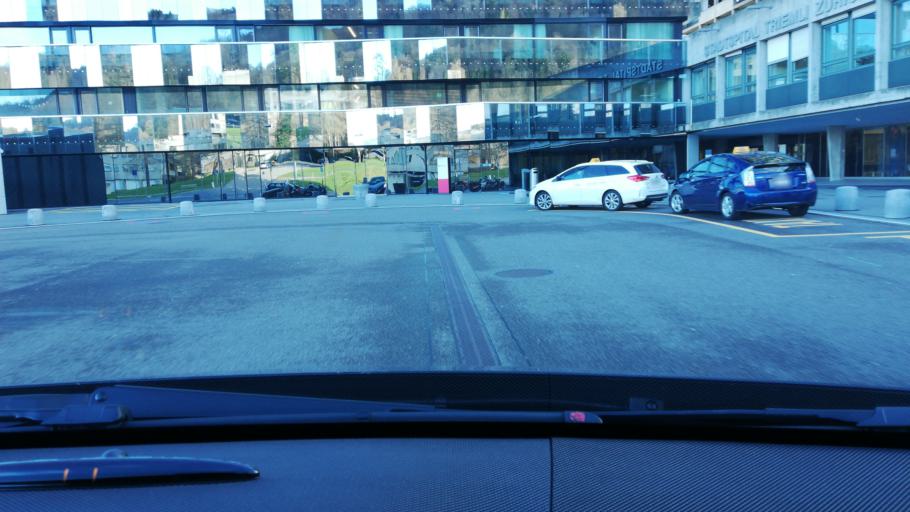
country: CH
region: Zurich
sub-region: Bezirk Zuerich
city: Zuerich (Kreis 3) / Friesenberg
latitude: 47.3660
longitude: 8.4971
